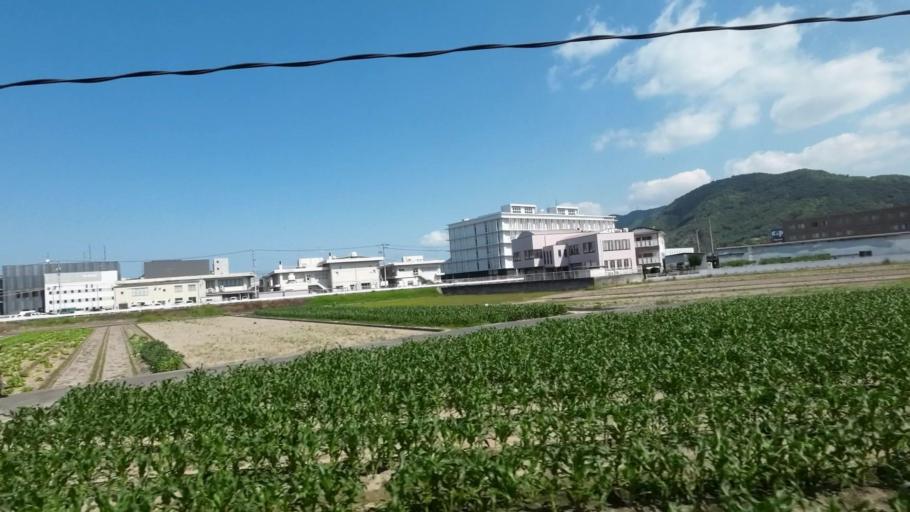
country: JP
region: Kagawa
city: Kan'onjicho
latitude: 34.1267
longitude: 133.6634
